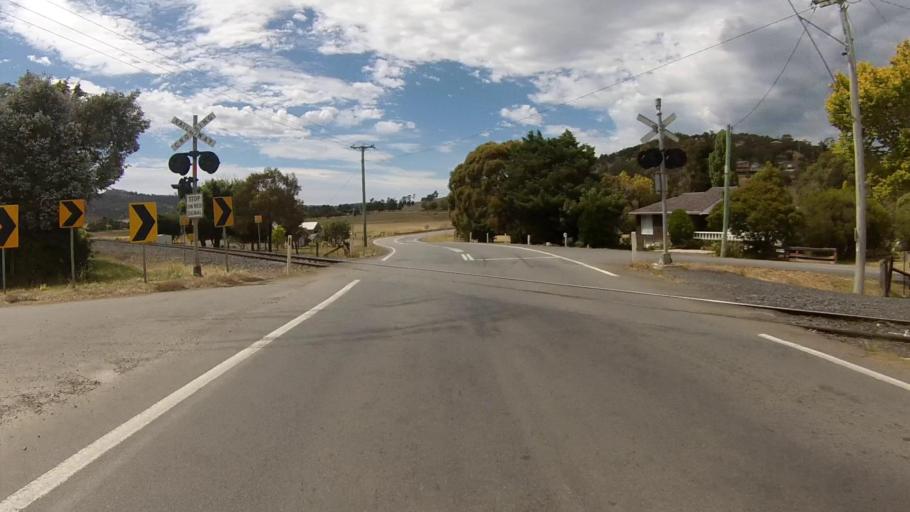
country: AU
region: Tasmania
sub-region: Brighton
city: Old Beach
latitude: -42.6898
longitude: 147.3312
